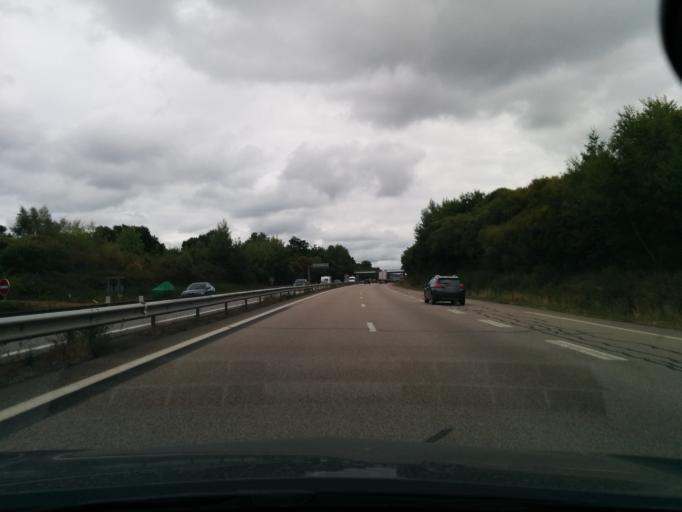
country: FR
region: Limousin
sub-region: Departement de la Haute-Vienne
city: Rilhac-Rancon
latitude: 45.9141
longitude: 1.2937
